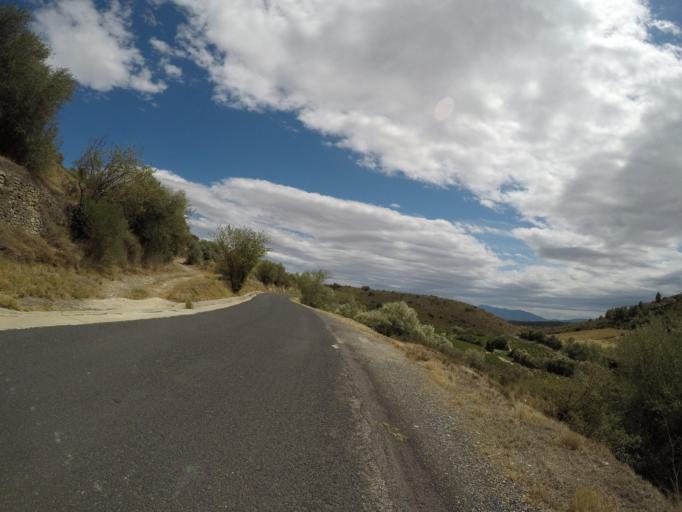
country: FR
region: Languedoc-Roussillon
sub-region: Departement des Pyrenees-Orientales
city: Baixas
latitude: 42.7564
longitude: 2.7654
